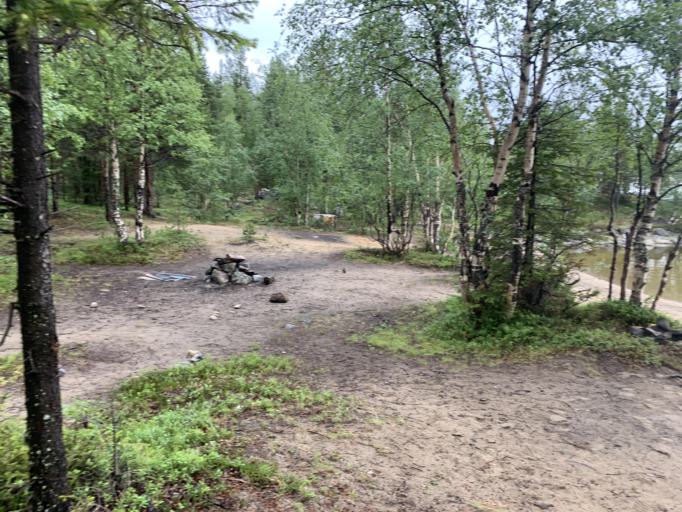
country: RU
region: Murmansk
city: Monchegorsk
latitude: 67.9490
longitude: 33.0237
